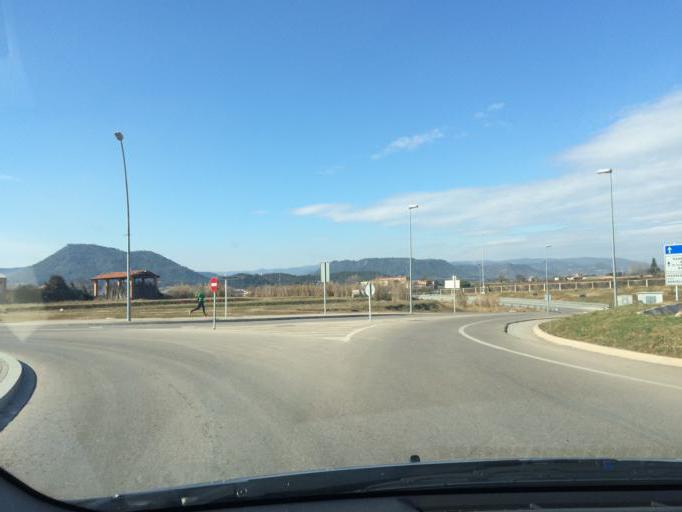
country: ES
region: Catalonia
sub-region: Provincia de Barcelona
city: Manresa
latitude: 41.7394
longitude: 1.8226
